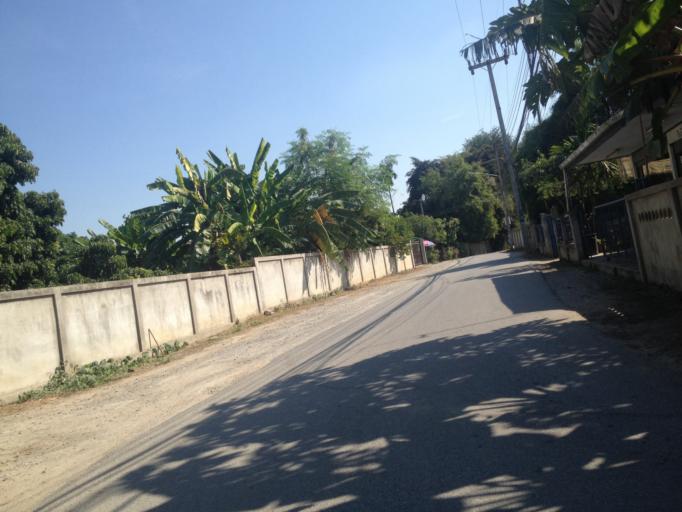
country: TH
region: Chiang Mai
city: Hang Dong
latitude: 18.6915
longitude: 98.9449
